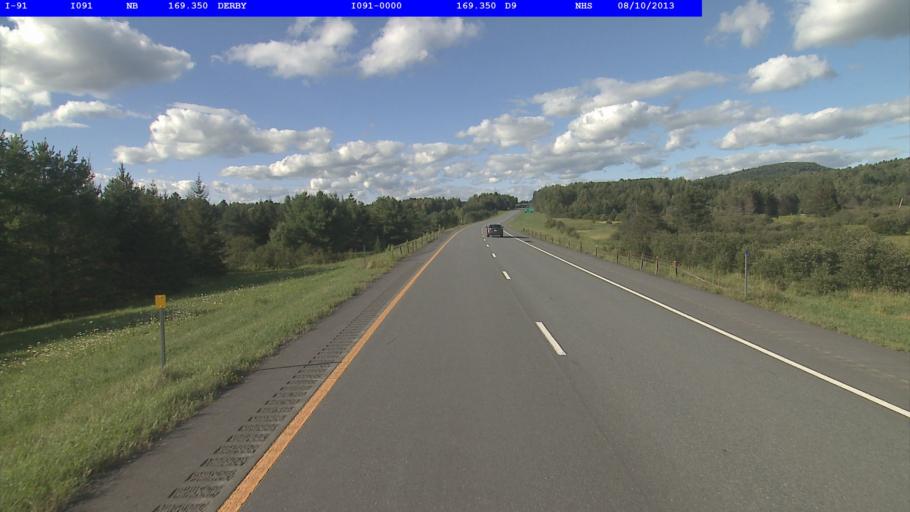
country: US
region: Vermont
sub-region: Orleans County
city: Newport
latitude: 44.9128
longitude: -72.1770
